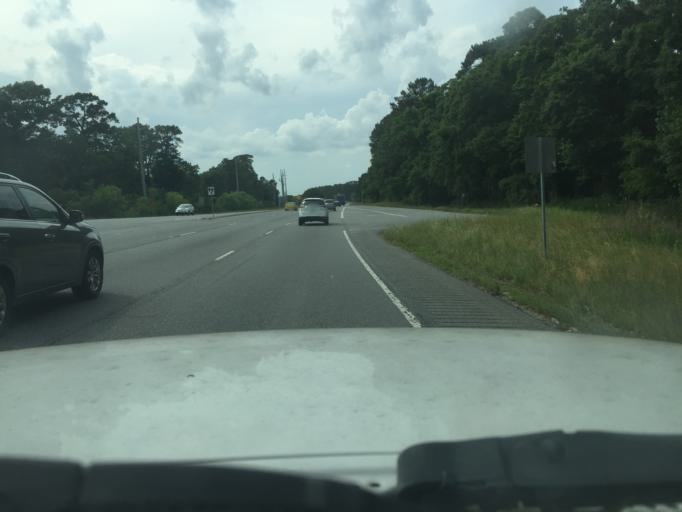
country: US
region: Georgia
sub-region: Chatham County
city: Whitemarsh Island
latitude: 32.0400
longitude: -80.9957
